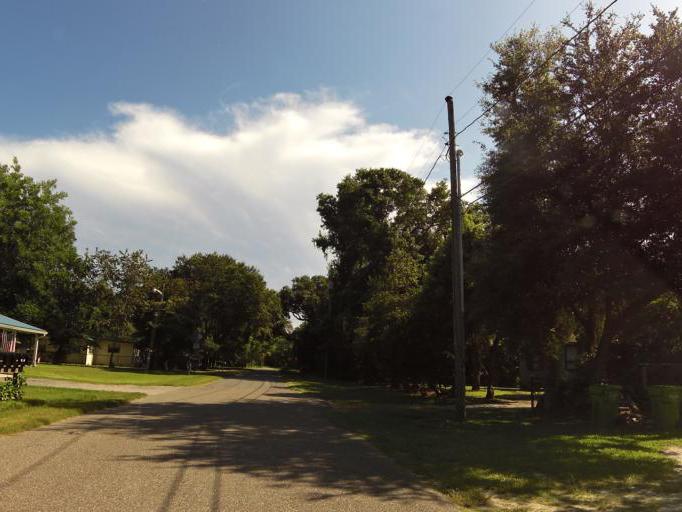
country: US
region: Florida
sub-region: Nassau County
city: Fernandina Beach
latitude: 30.6559
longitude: -81.4645
